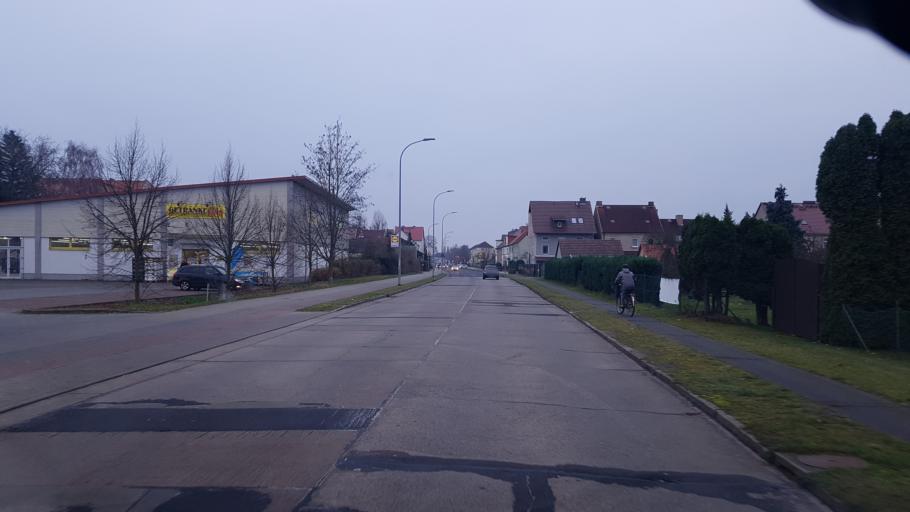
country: DE
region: Brandenburg
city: Guben
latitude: 51.9513
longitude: 14.7025
